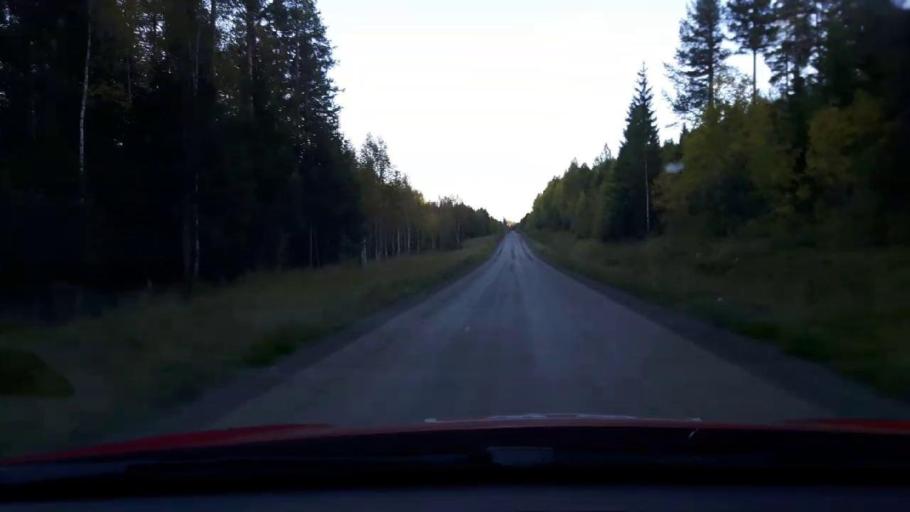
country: SE
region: Jaemtland
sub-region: OEstersunds Kommun
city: Brunflo
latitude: 62.9406
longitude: 14.9896
